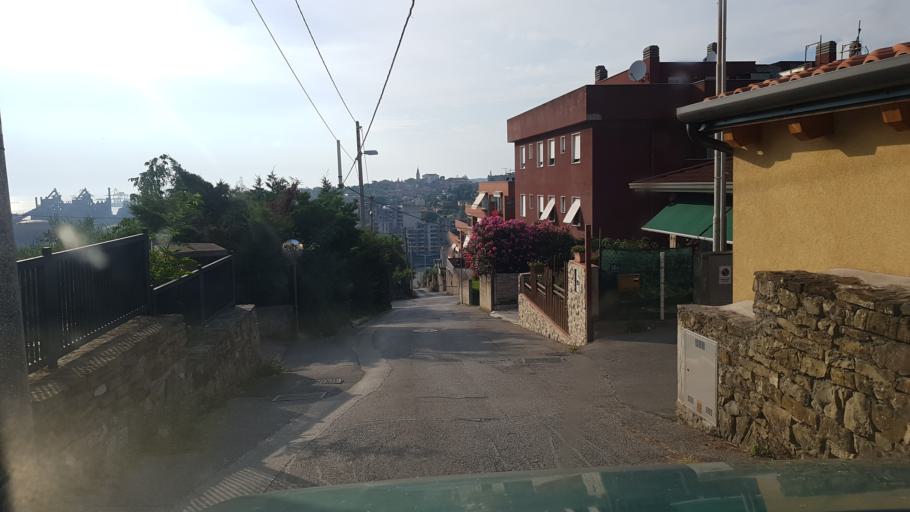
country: IT
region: Friuli Venezia Giulia
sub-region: Provincia di Trieste
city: Trieste
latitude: 45.6180
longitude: 13.7915
